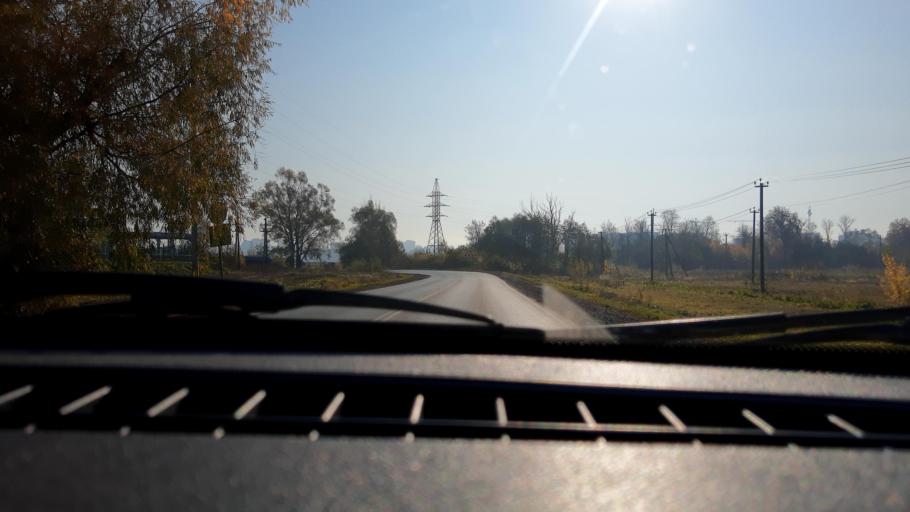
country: RU
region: Bashkortostan
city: Mikhaylovka
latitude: 54.8004
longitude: 55.8361
